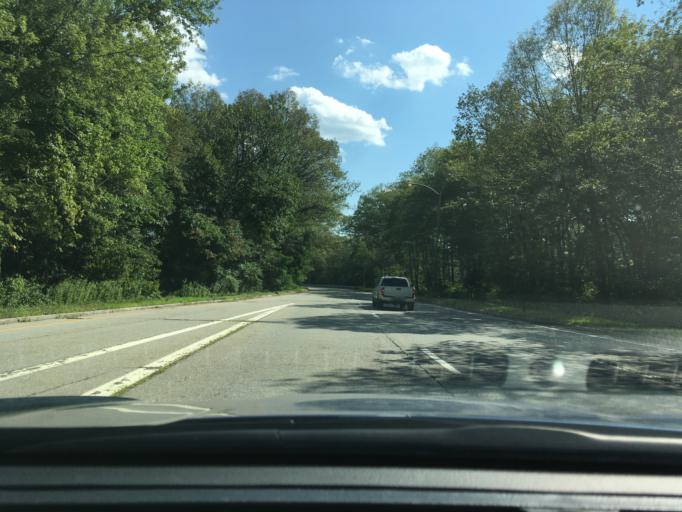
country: US
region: Rhode Island
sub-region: Kent County
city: West Warwick
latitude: 41.7343
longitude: -71.4813
